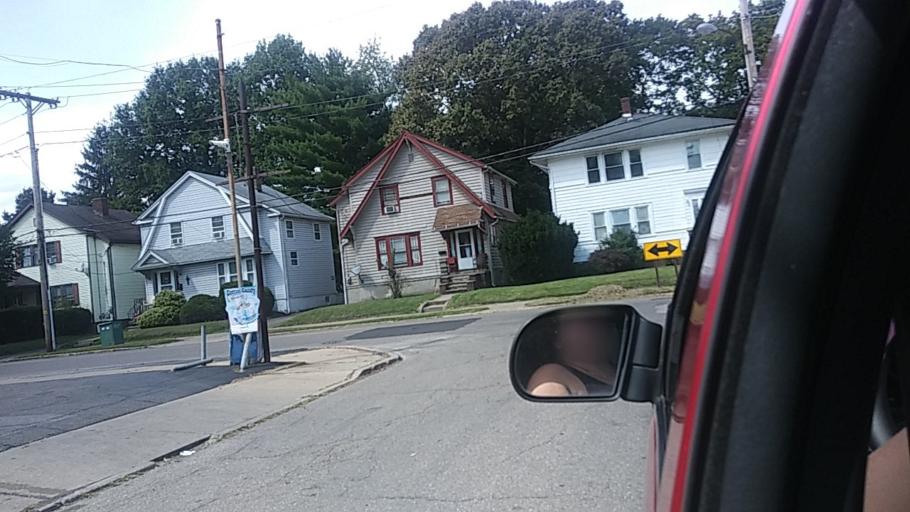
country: US
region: Ohio
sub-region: Summit County
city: Akron
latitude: 41.0921
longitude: -81.5506
